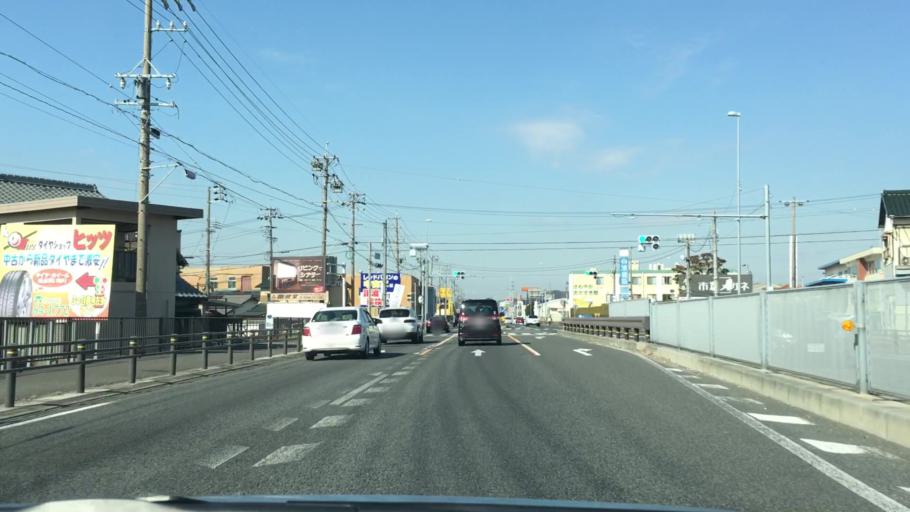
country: JP
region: Aichi
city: Okazaki
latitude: 34.9379
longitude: 137.1951
